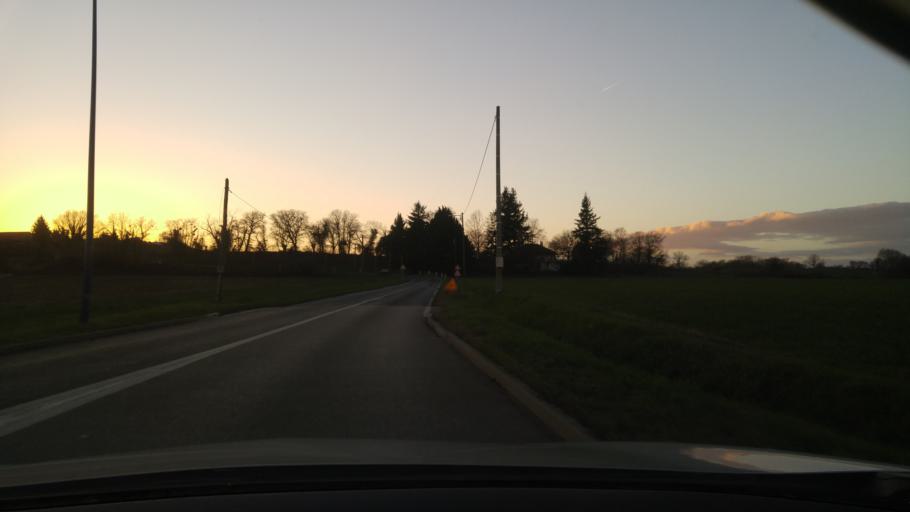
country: FR
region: Rhone-Alpes
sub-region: Departement de l'Isere
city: Satolas-et-Bonce
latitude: 45.7150
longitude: 5.1545
